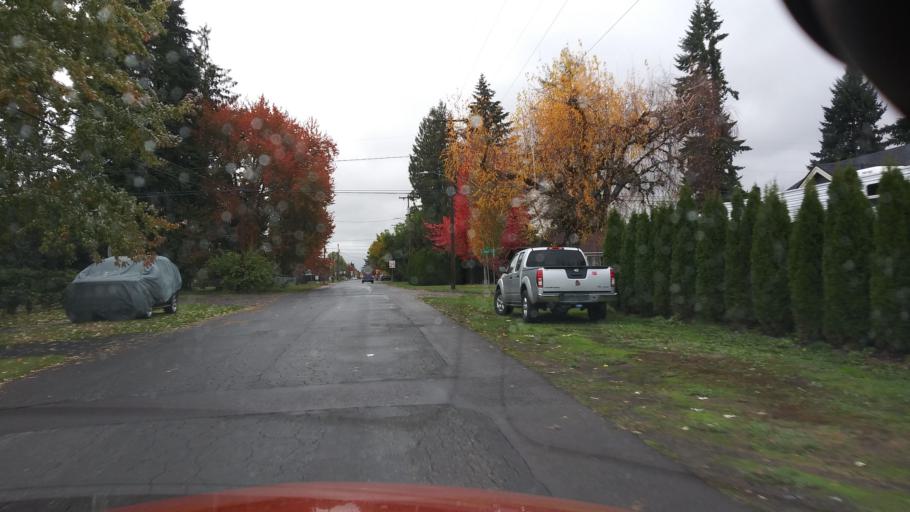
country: US
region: Oregon
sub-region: Washington County
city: Cornelius
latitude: 45.5171
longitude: -123.0570
